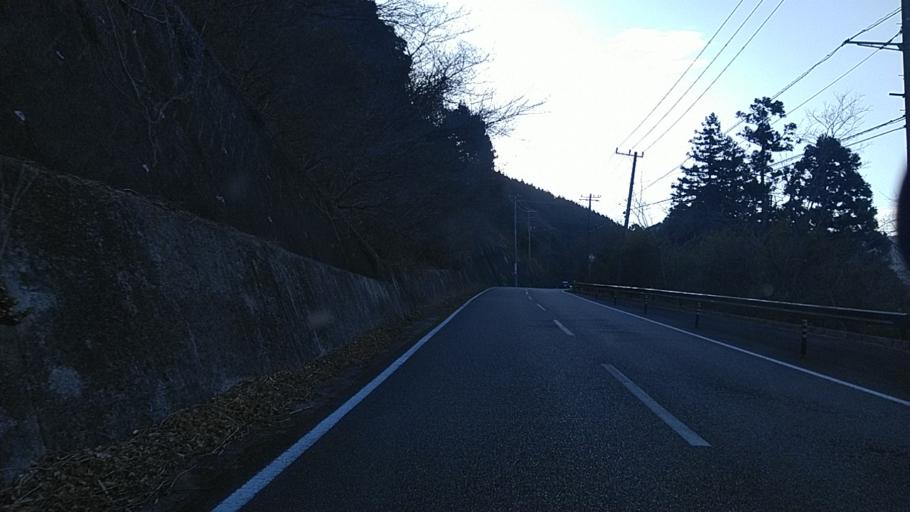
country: JP
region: Chiba
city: Kimitsu
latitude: 35.2615
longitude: 139.9325
